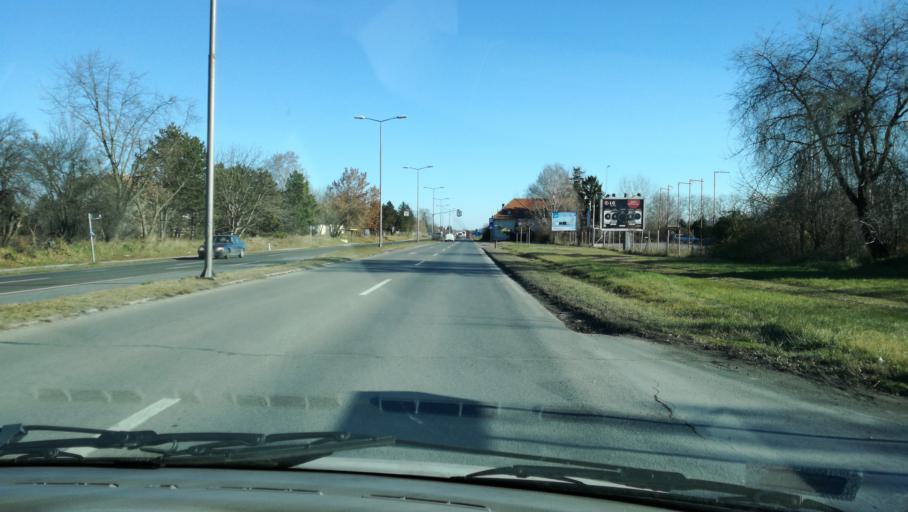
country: RS
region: Autonomna Pokrajina Vojvodina
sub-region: Severnobacki Okrug
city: Subotica
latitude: 46.1033
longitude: 19.7112
